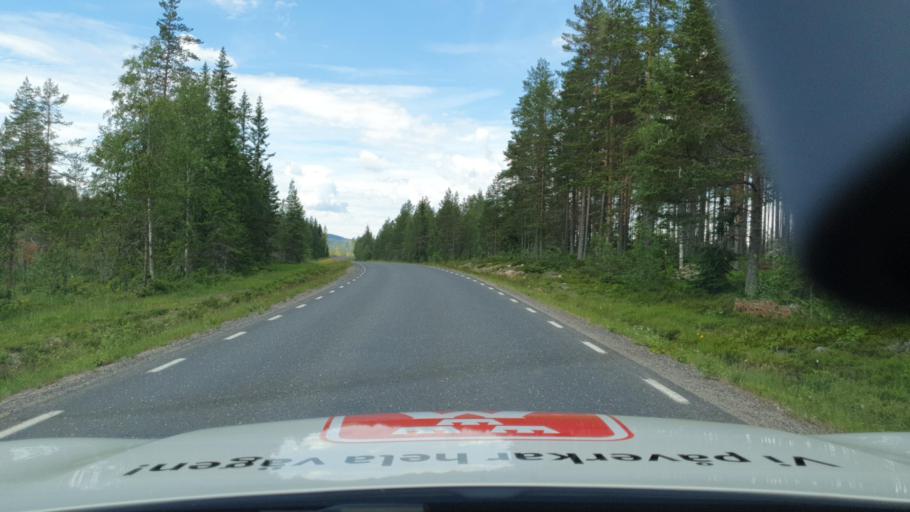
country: SE
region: Vaermland
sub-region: Torsby Kommun
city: Torsby
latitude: 60.5425
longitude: 12.7980
